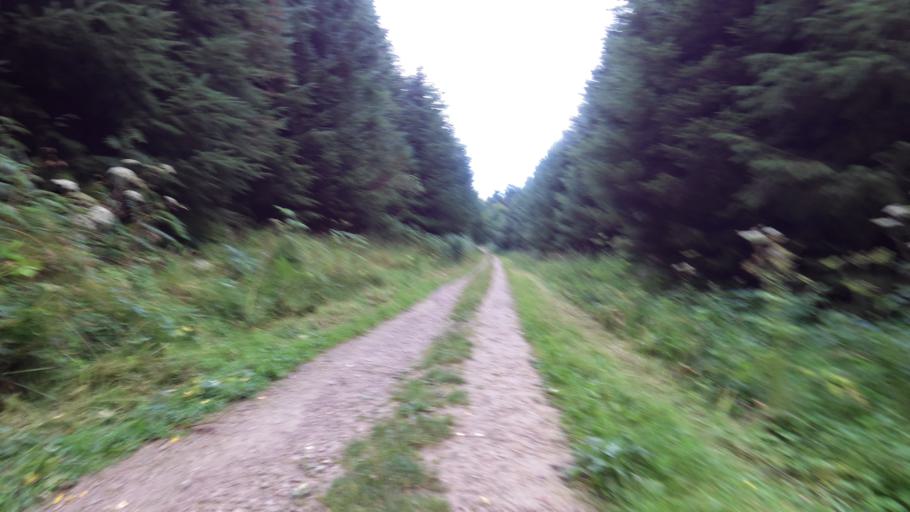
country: GB
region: England
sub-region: North Yorkshire
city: Thornton Dale
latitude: 54.2915
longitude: -0.6709
